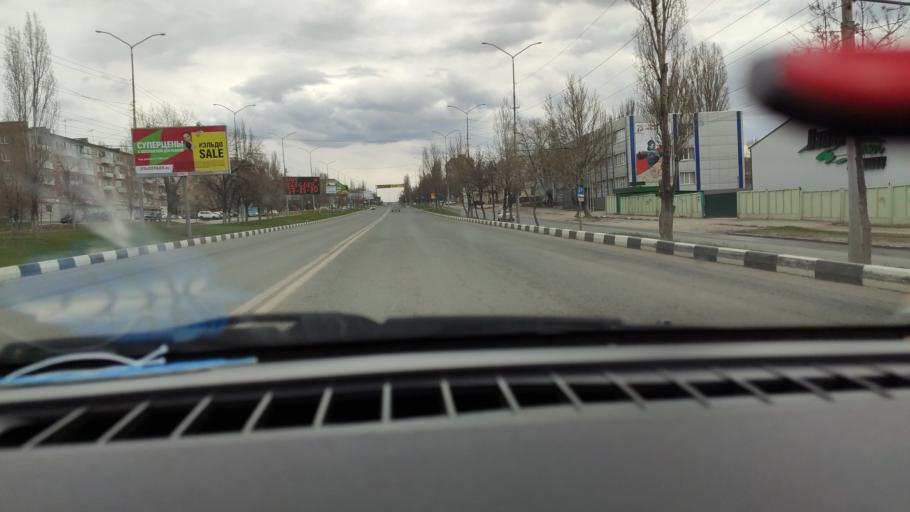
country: RU
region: Saratov
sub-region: Saratovskiy Rayon
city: Saratov
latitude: 51.6021
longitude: 45.9687
